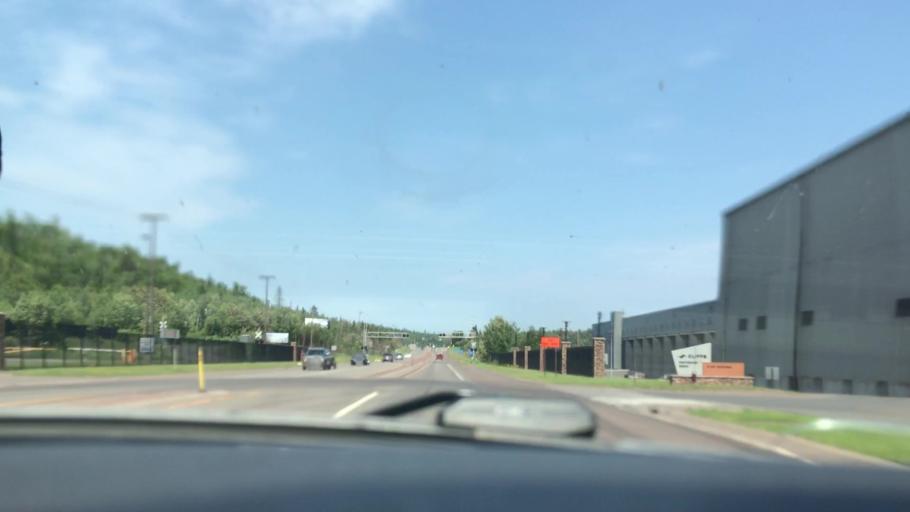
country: US
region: Minnesota
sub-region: Lake County
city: Silver Bay
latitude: 47.2895
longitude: -91.2626
